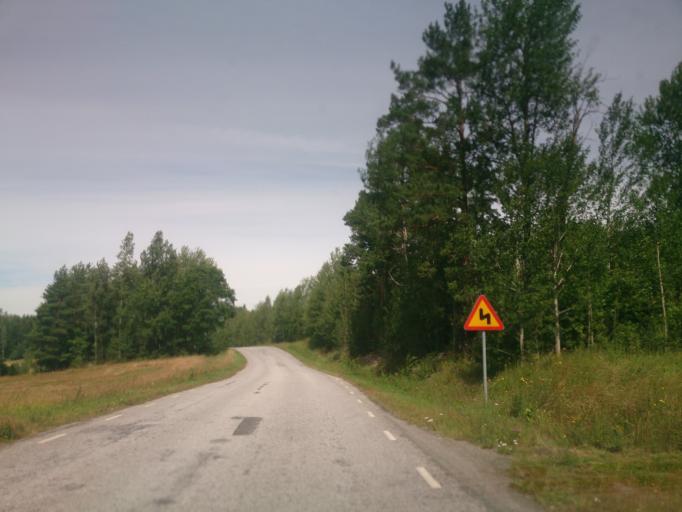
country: SE
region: OEstergoetland
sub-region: Valdemarsviks Kommun
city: Gusum
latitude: 58.3337
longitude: 16.5851
